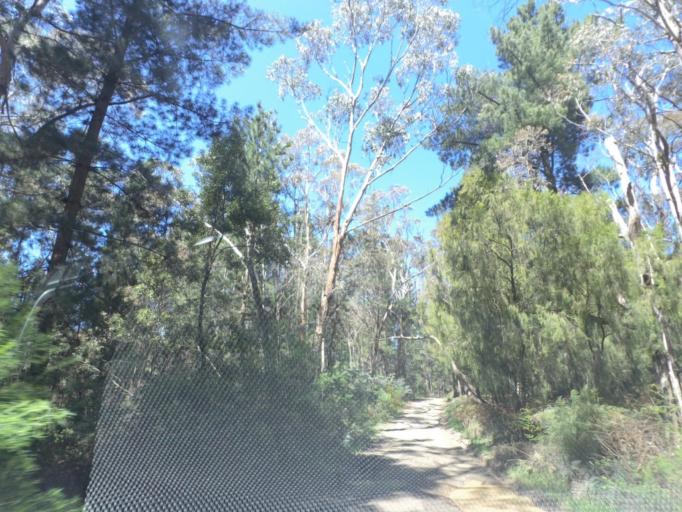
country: AU
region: Victoria
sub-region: Hume
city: Sunbury
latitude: -37.3918
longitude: 144.5536
